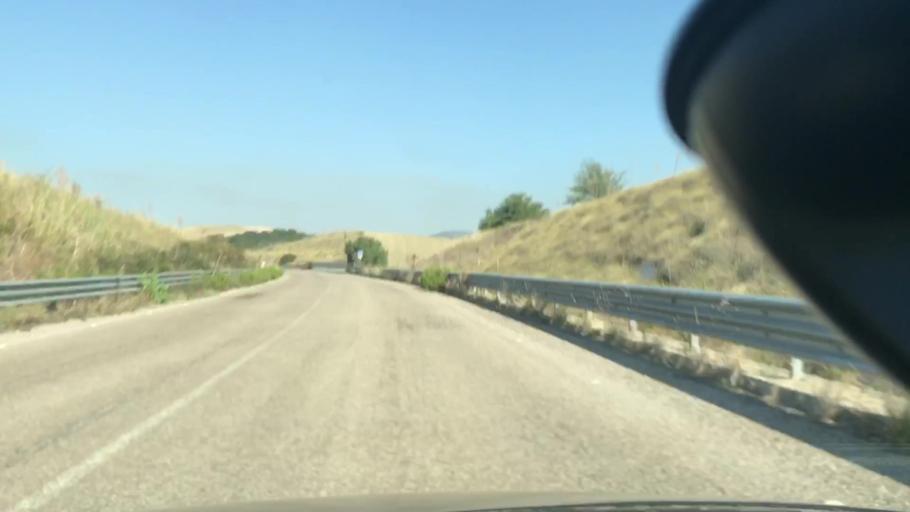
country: IT
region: Basilicate
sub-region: Provincia di Matera
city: La Martella
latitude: 40.6880
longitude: 16.4484
